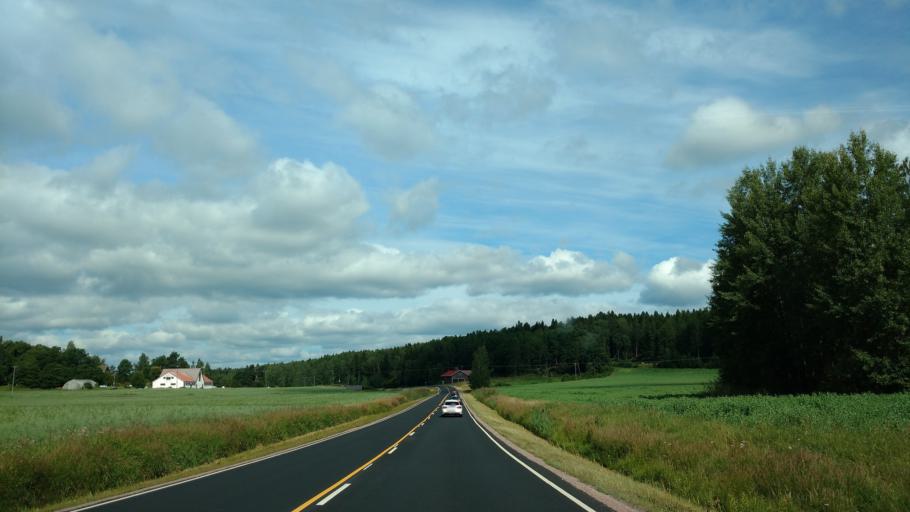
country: FI
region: Varsinais-Suomi
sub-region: Salo
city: Saerkisalo
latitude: 60.1803
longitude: 22.8995
